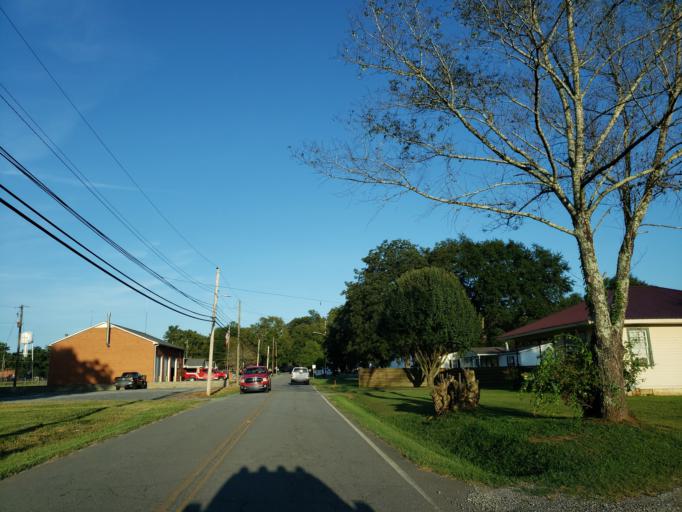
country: US
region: Georgia
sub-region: Bartow County
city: Euharlee
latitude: 34.2354
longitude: -84.9489
